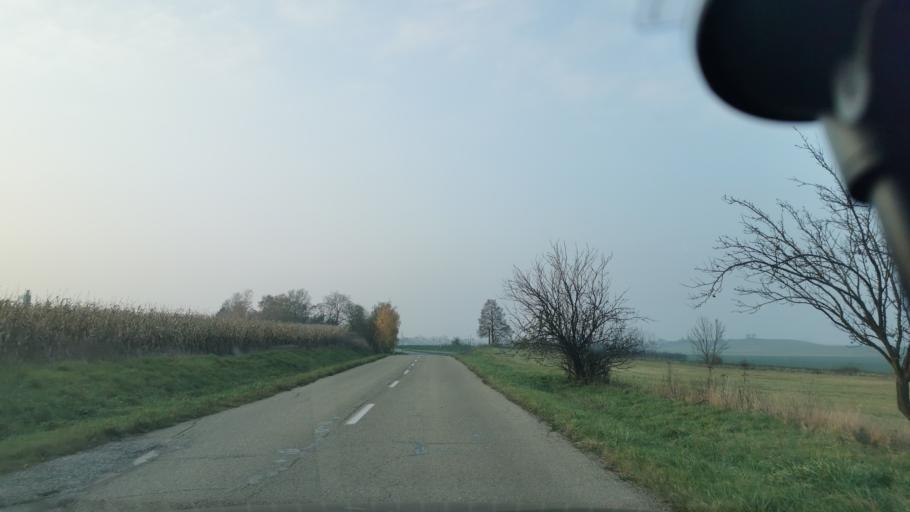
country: SK
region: Trnavsky
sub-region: Okres Skalica
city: Holic
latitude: 48.8024
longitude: 17.1835
